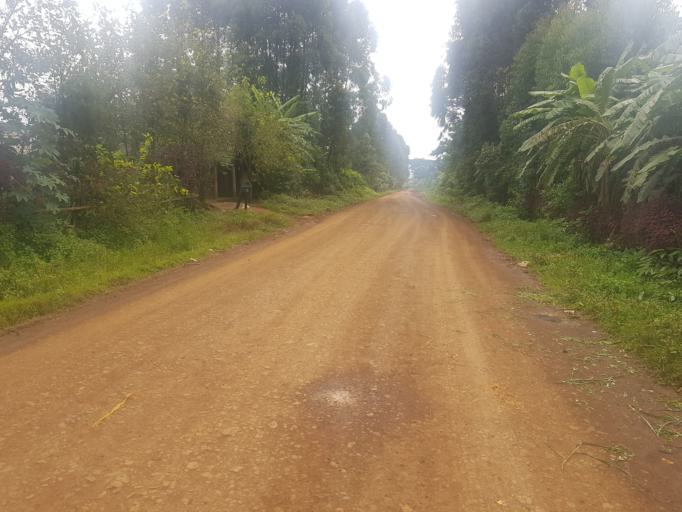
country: ET
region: Oromiya
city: Gore
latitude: 7.8983
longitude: 35.4947
